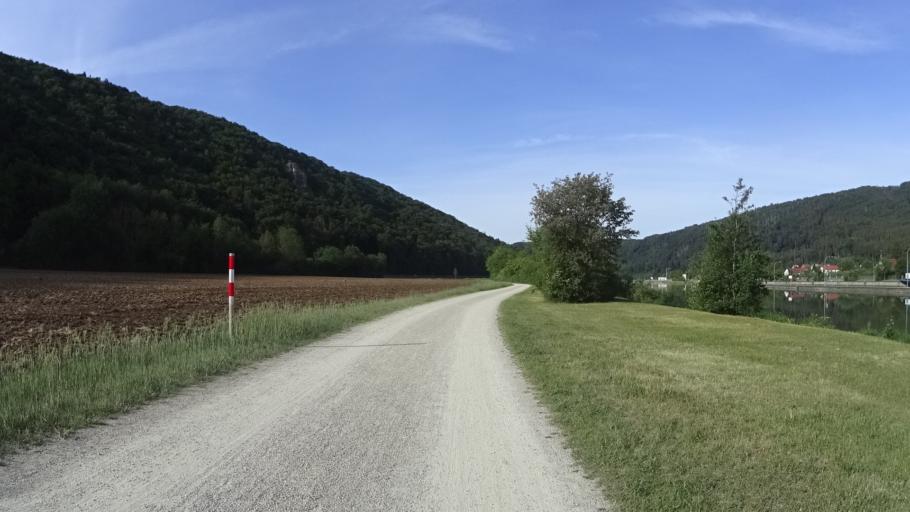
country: DE
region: Bavaria
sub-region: Lower Bavaria
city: Riedenburg
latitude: 48.9783
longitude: 11.6936
